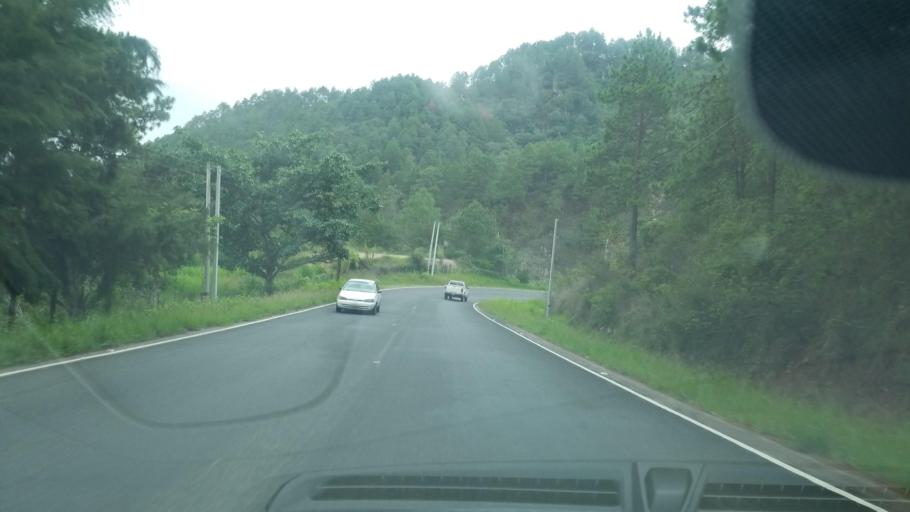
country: HN
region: Ocotepeque
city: Sinuapa
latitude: 14.4530
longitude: -89.1411
